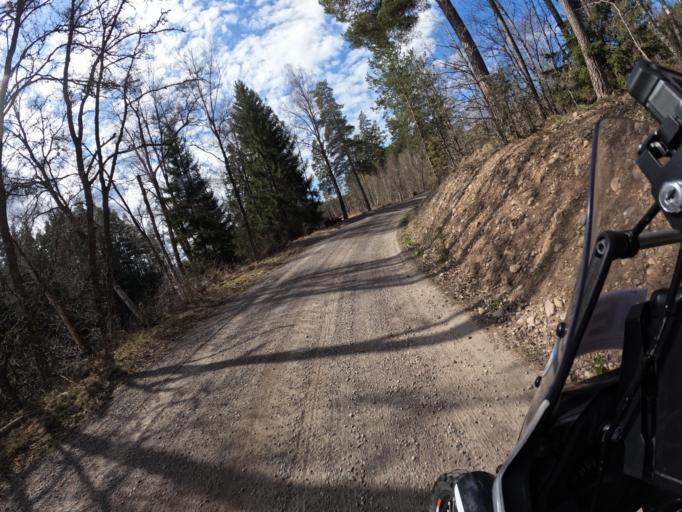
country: SE
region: Joenkoeping
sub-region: Mullsjo Kommun
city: Mullsjoe
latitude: 57.9935
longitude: 13.8401
